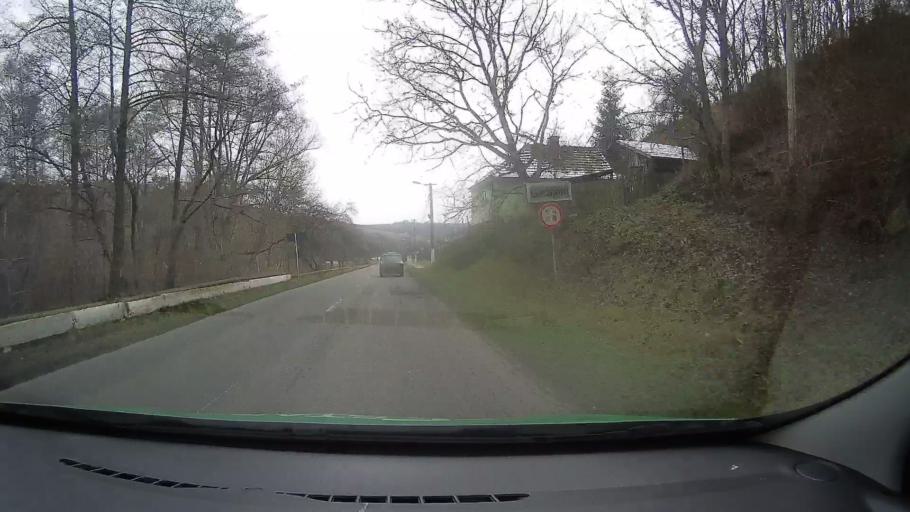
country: RO
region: Hunedoara
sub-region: Comuna Geoagiu
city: Geoagiu
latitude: 45.9350
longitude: 23.1912
